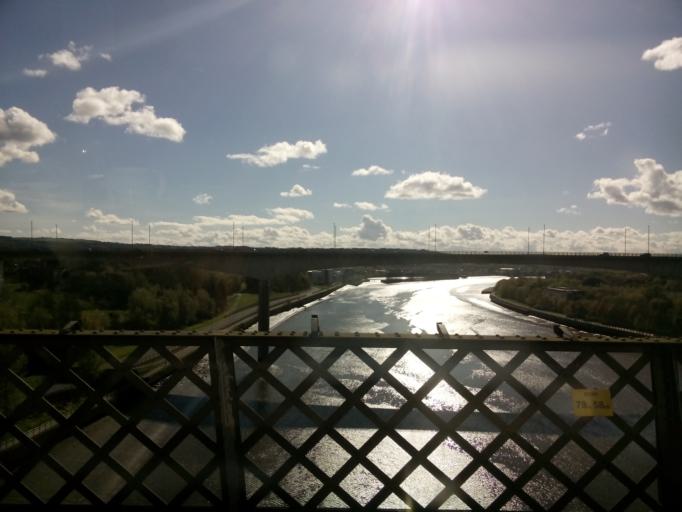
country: GB
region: England
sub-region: Newcastle upon Tyne
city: Newcastle upon Tyne
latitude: 54.9628
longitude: -1.6159
